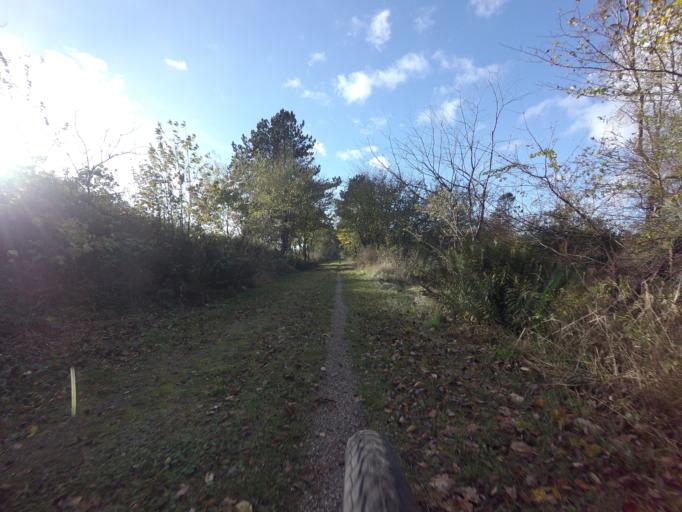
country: DK
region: Central Jutland
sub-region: Norddjurs Kommune
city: Grenaa
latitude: 56.4957
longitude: 10.7207
